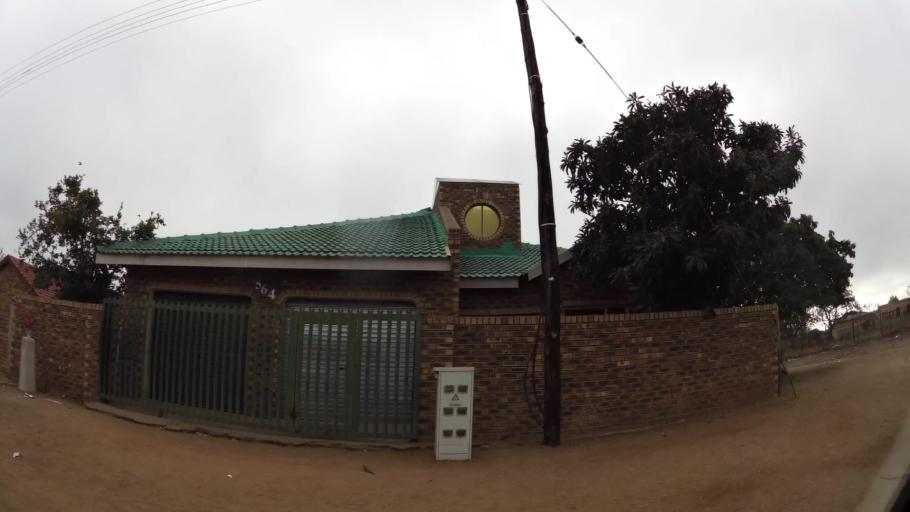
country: ZA
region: Limpopo
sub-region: Capricorn District Municipality
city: Polokwane
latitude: -23.8397
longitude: 29.3882
